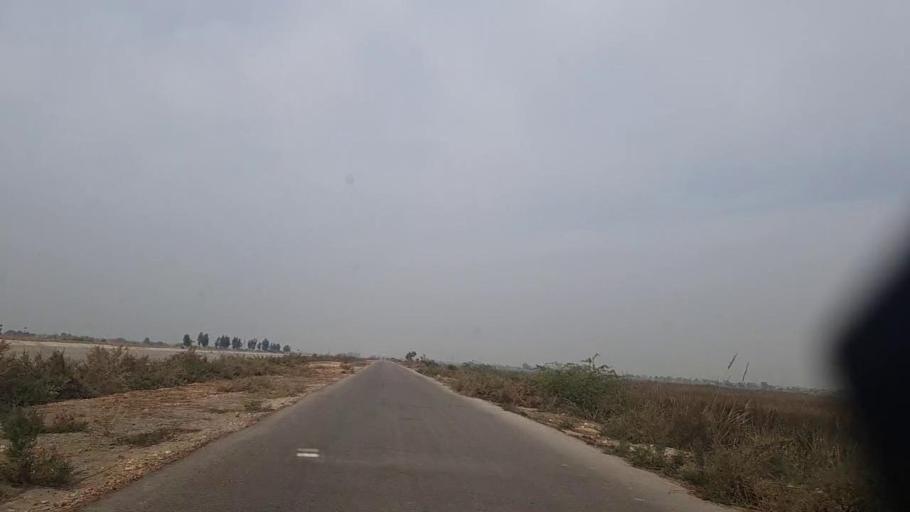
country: PK
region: Sindh
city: Sakrand
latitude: 26.2668
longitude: 68.2382
